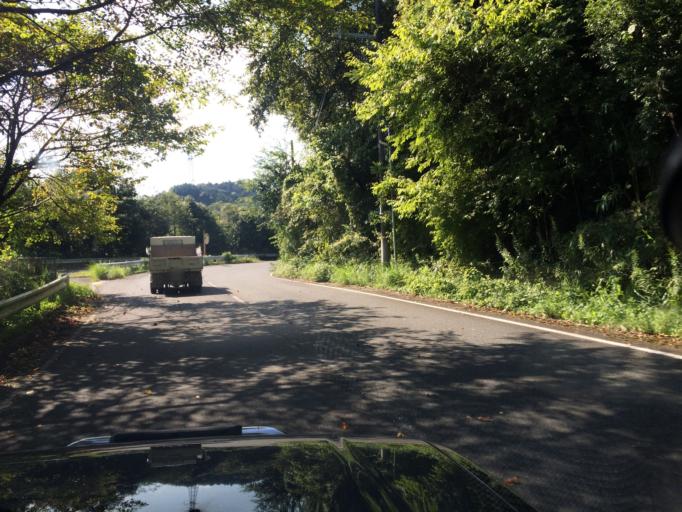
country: JP
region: Mie
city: Nabari
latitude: 34.7000
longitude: 135.9744
